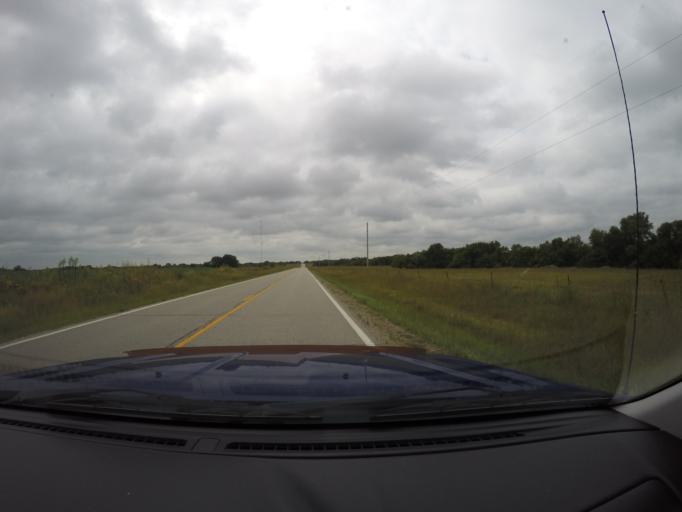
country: US
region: Kansas
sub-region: Morris County
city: Council Grove
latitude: 38.8409
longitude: -96.5492
